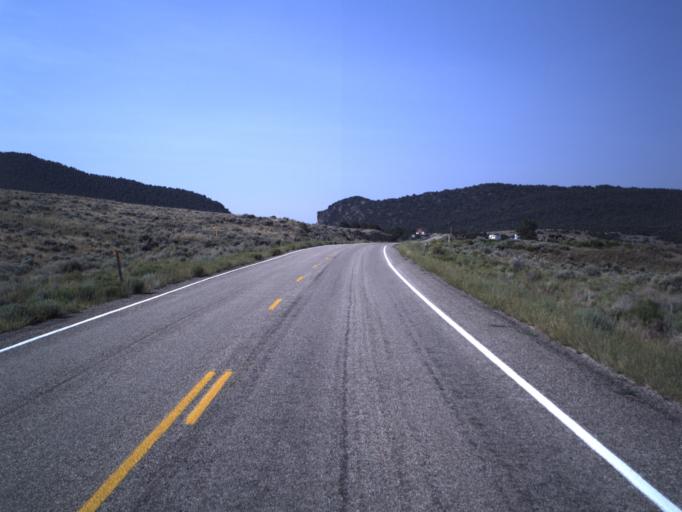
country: US
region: Utah
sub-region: Daggett County
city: Manila
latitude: 40.9688
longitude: -109.4648
